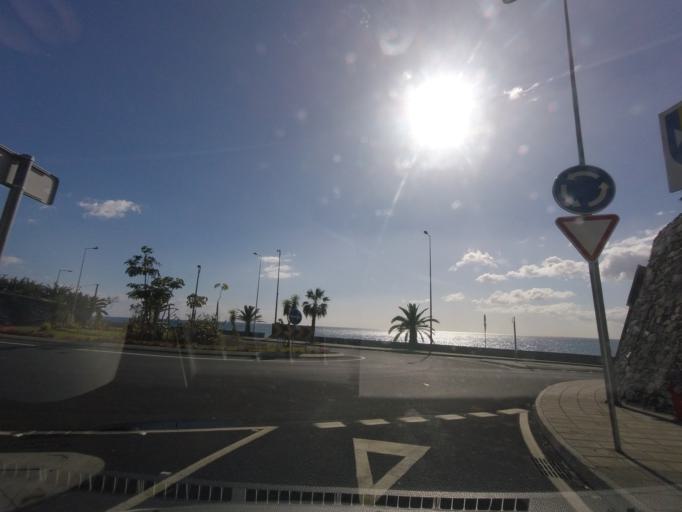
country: PT
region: Madeira
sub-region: Calheta
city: Arco da Calheta
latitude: 32.7033
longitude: -17.1318
